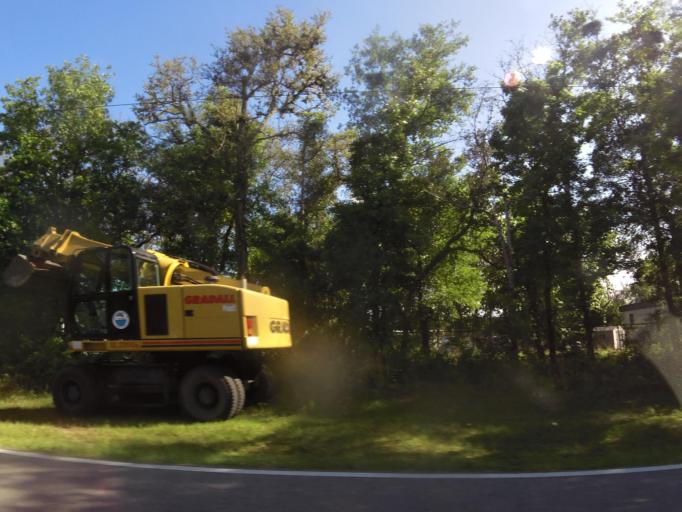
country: US
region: Florida
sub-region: Duval County
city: Jacksonville
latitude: 30.4347
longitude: -81.5676
